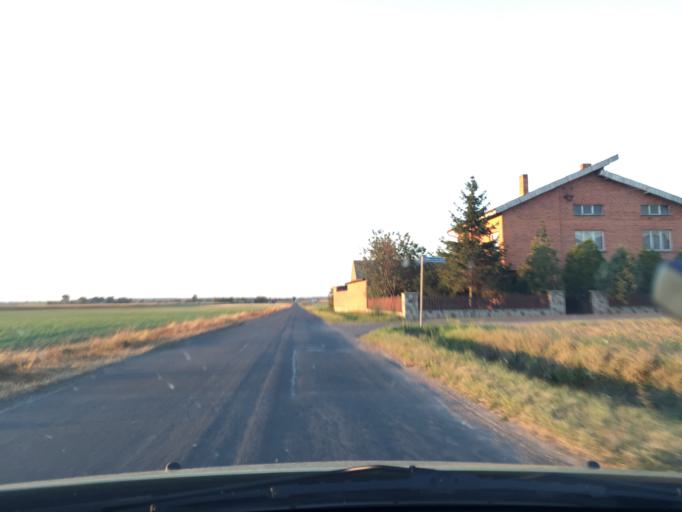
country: PL
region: Greater Poland Voivodeship
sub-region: Powiat jarocinski
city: Golina
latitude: 51.8798
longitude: 17.5342
